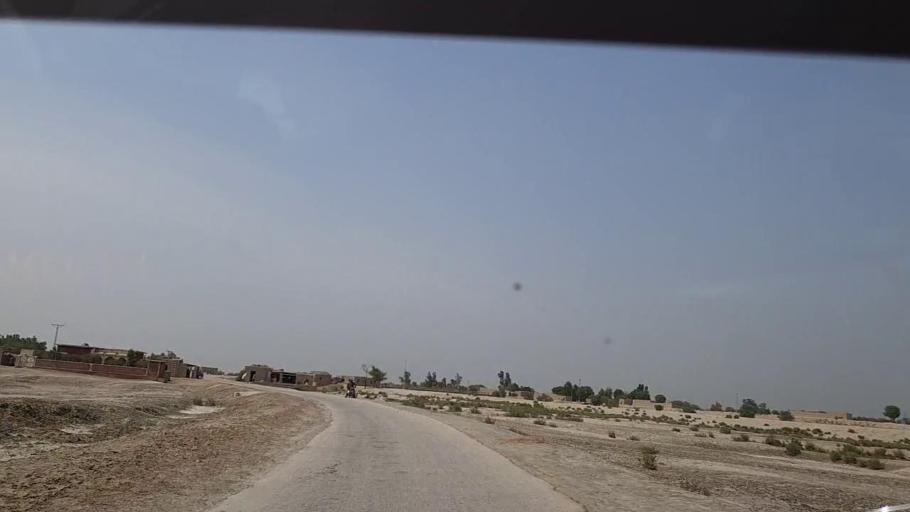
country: PK
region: Sindh
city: Khairpur Nathan Shah
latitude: 27.0722
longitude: 67.6514
